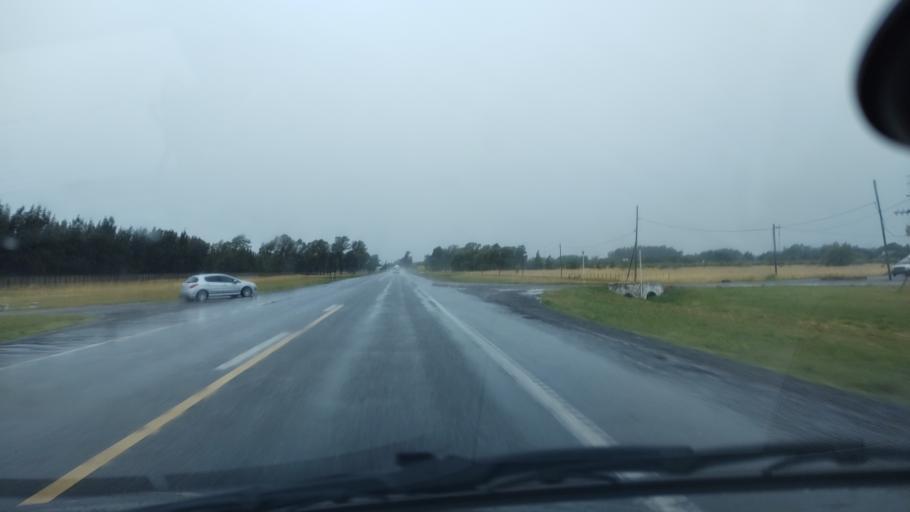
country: AR
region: Buenos Aires
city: Canuelas
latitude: -35.0564
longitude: -58.7899
